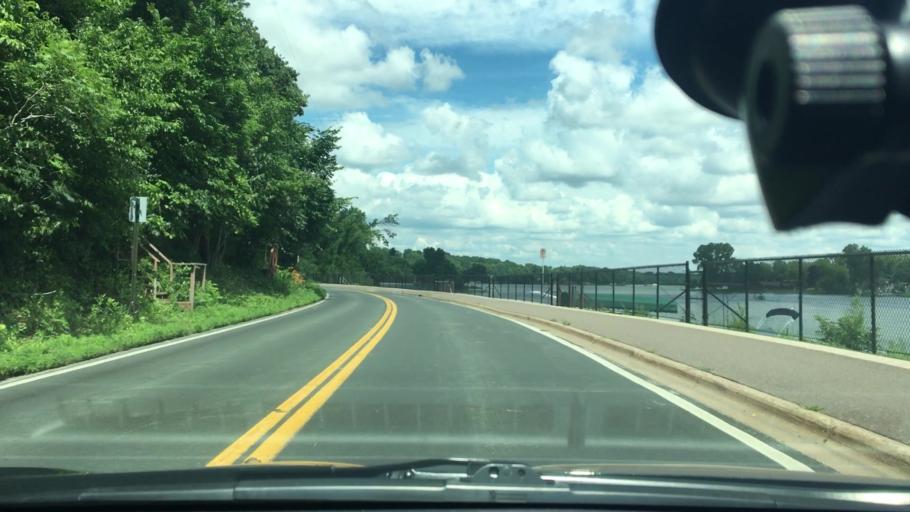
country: US
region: Minnesota
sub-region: Hennepin County
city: Plymouth
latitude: 44.9973
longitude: -93.4277
